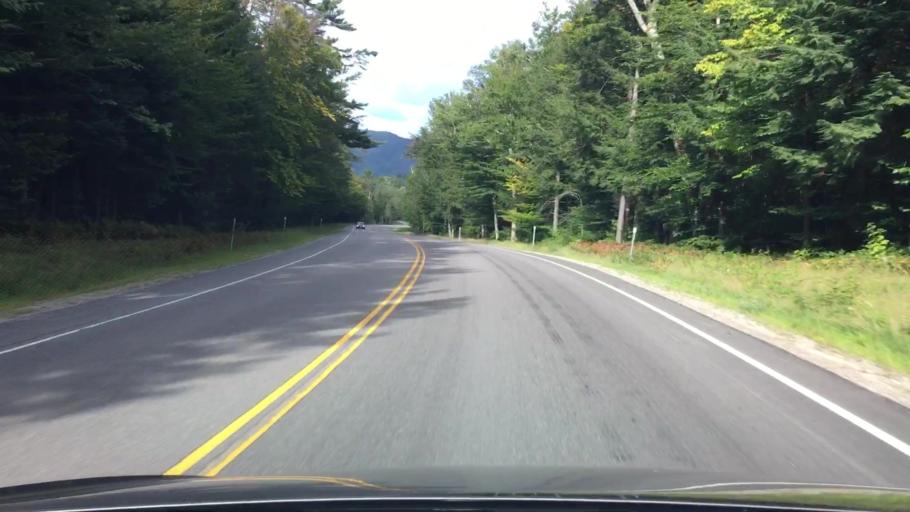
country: US
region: New Hampshire
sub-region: Carroll County
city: Tamworth
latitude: 43.9919
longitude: -71.2906
